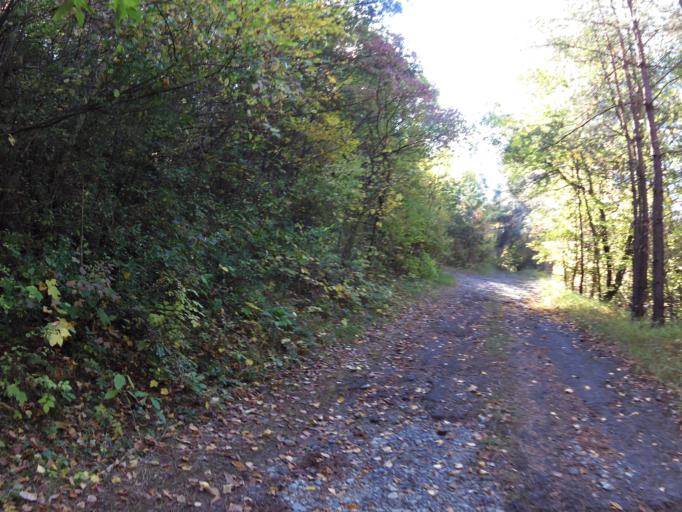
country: DE
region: Bavaria
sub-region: Regierungsbezirk Unterfranken
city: Eibelstadt
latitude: 49.7247
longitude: 9.9872
